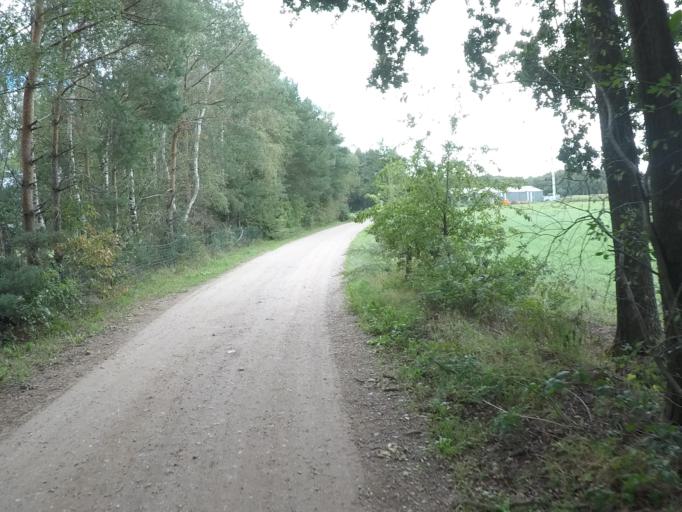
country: BE
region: Flanders
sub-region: Provincie Antwerpen
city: Vorselaar
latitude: 51.2187
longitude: 4.7711
